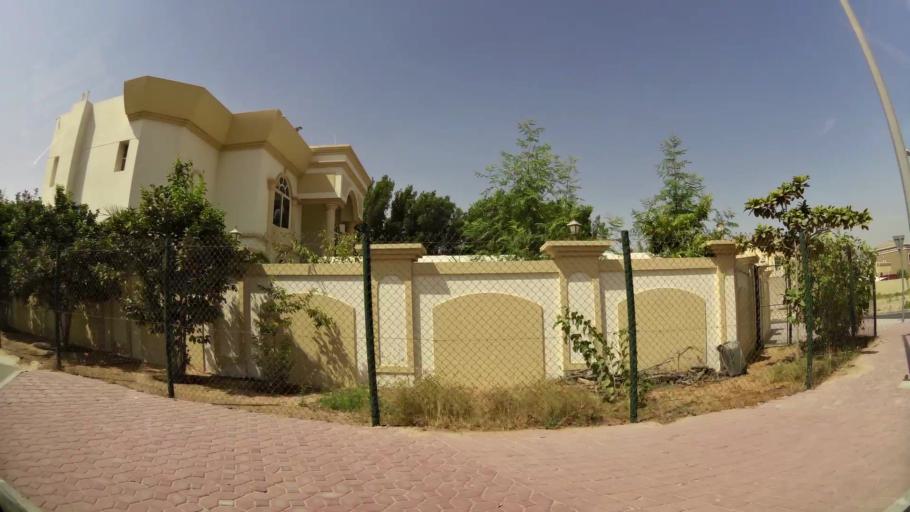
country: AE
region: Ash Shariqah
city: Sharjah
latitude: 25.2026
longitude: 55.4326
